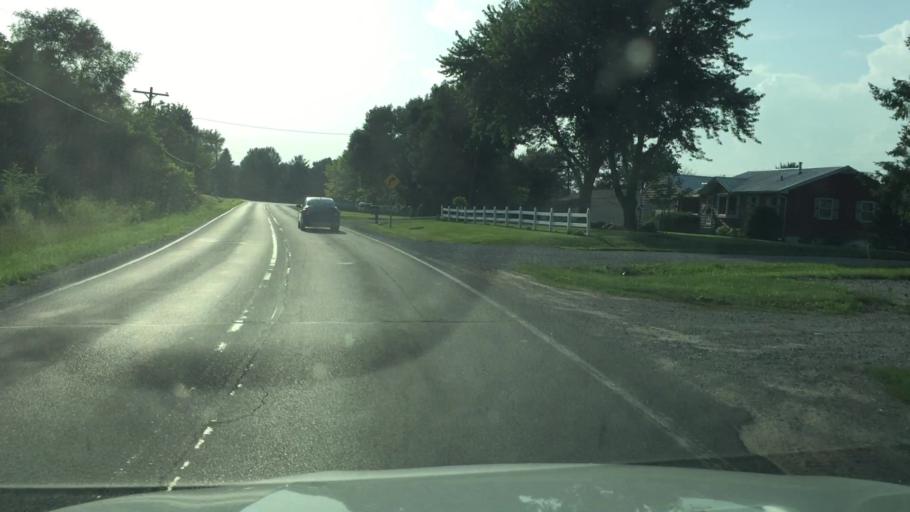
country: US
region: Iowa
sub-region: Linn County
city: Ely
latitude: 41.8406
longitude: -91.6418
